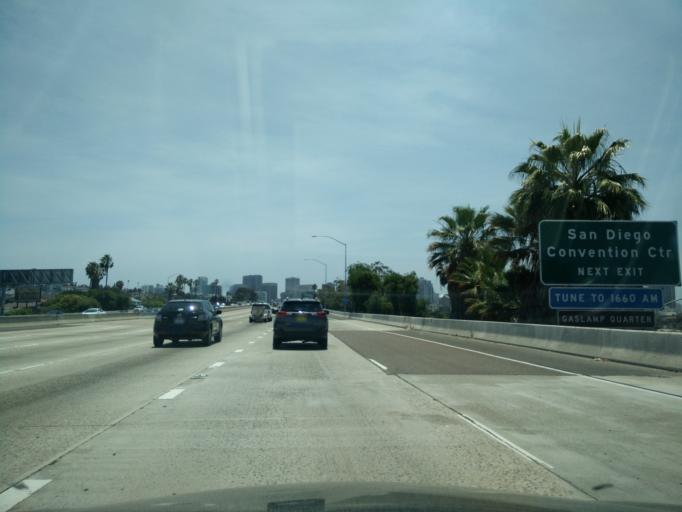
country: US
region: California
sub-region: San Diego County
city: San Diego
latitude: 32.7308
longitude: -117.1712
